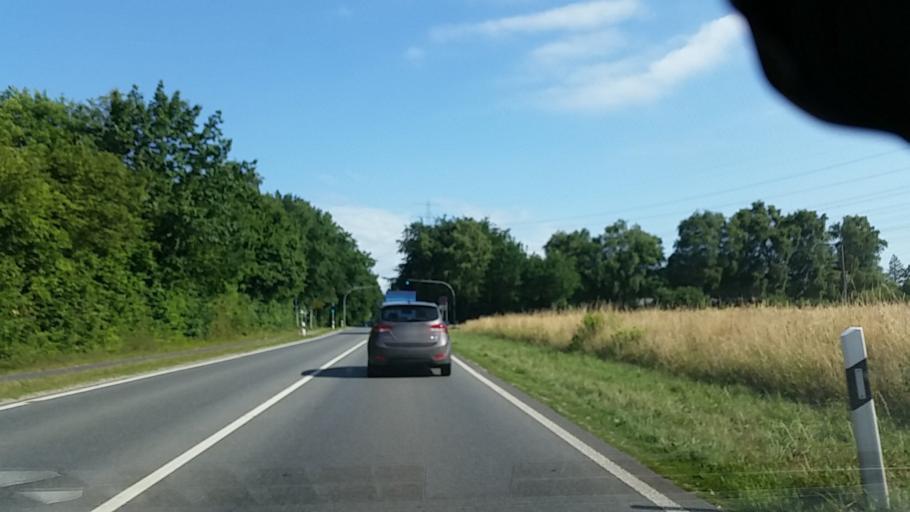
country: DE
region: Schleswig-Holstein
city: Tangstedt
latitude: 53.7255
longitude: 10.0261
